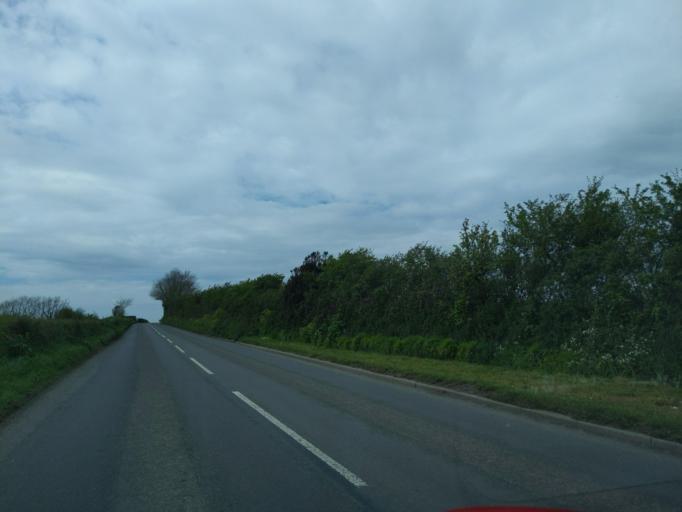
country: GB
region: England
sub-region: Cornwall
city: Wadebridge
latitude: 50.5352
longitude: -4.8480
